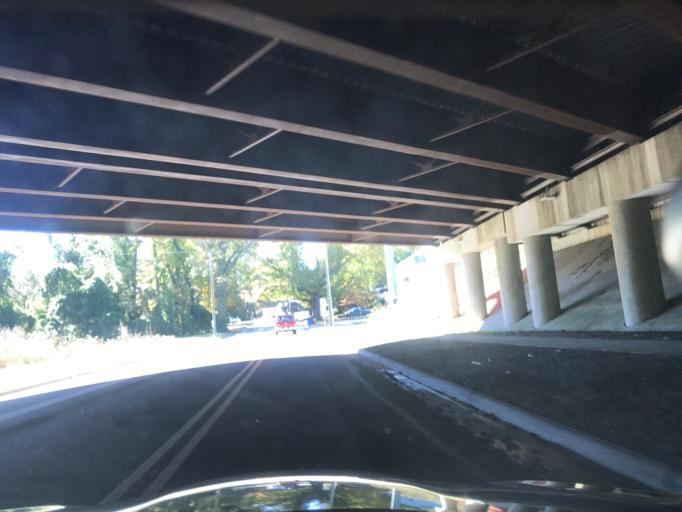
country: US
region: North Carolina
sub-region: Durham County
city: Durham
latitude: 36.0180
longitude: -78.8984
